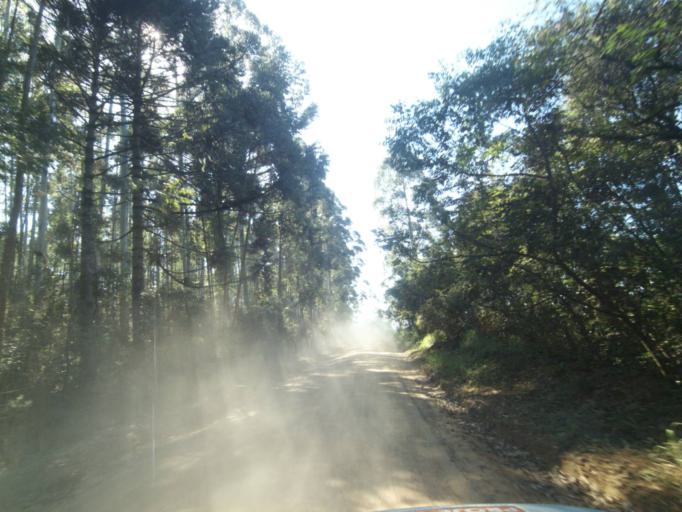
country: BR
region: Parana
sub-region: Tibagi
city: Tibagi
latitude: -24.5523
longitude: -50.6214
